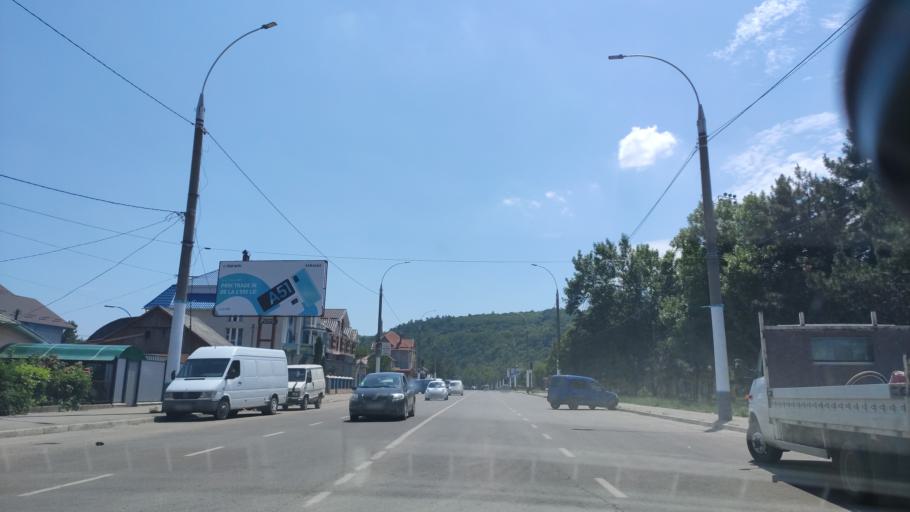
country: MD
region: Raionul Soroca
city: Soroca
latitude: 48.1482
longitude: 28.3021
